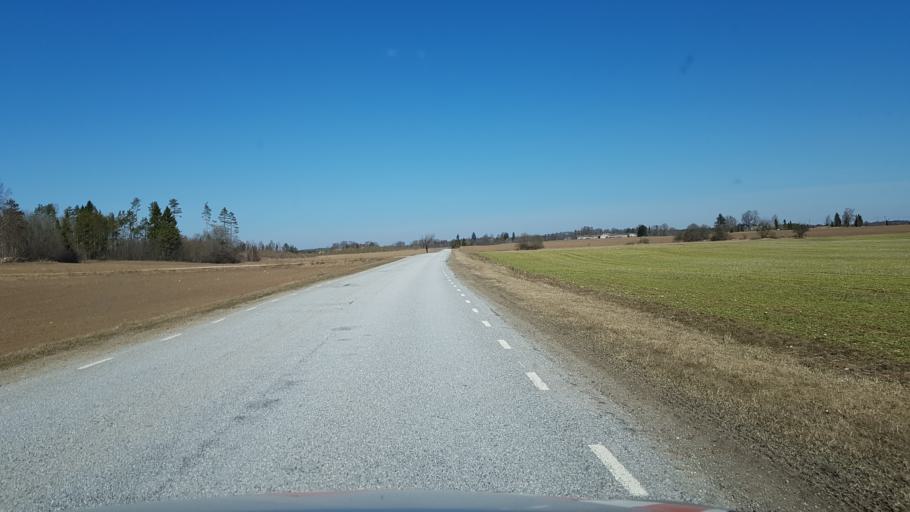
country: EE
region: Jaervamaa
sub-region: Koeru vald
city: Koeru
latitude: 59.0244
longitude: 26.0884
